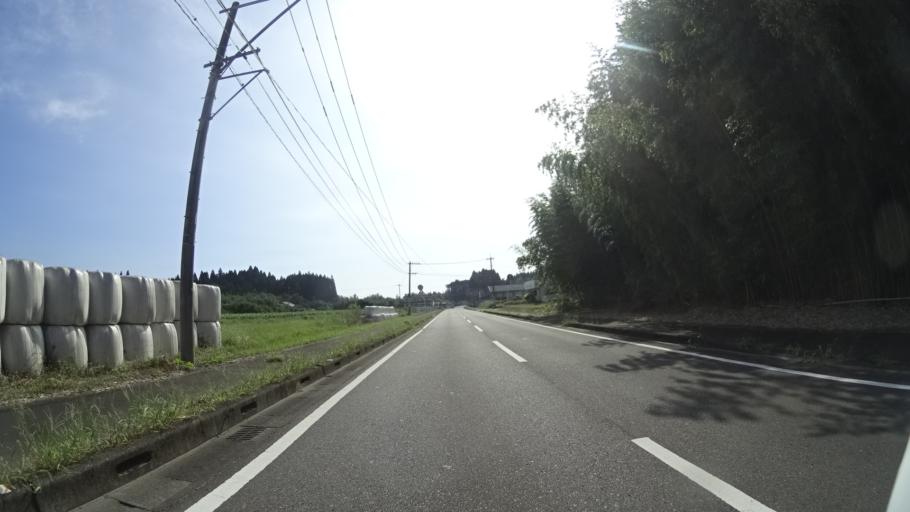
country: JP
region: Kagoshima
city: Okuchi-shinohara
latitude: 32.0413
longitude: 130.7890
